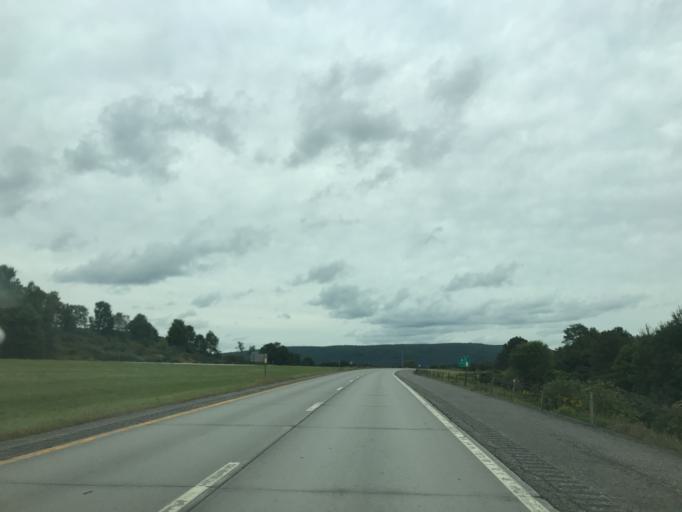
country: US
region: New York
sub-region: Otsego County
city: Oneonta
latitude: 42.4726
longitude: -74.9969
